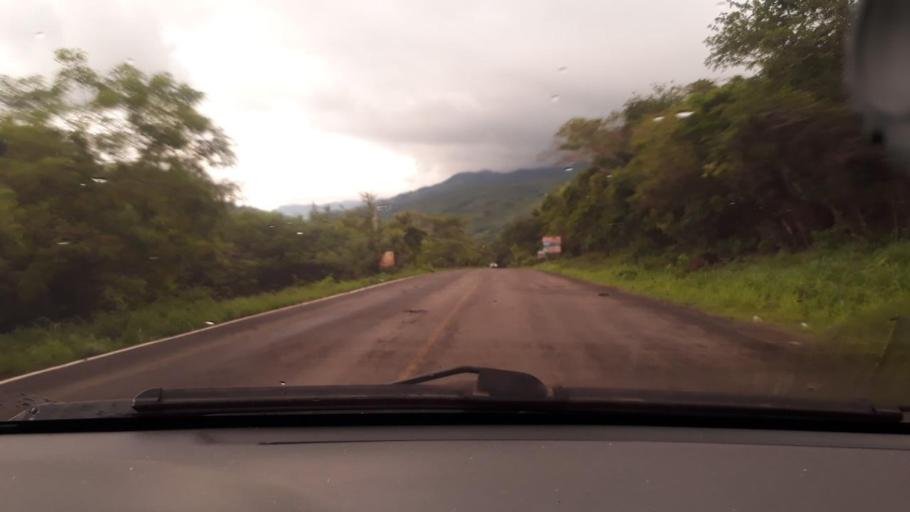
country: GT
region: Jutiapa
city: Comapa
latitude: 14.0768
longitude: -89.9562
